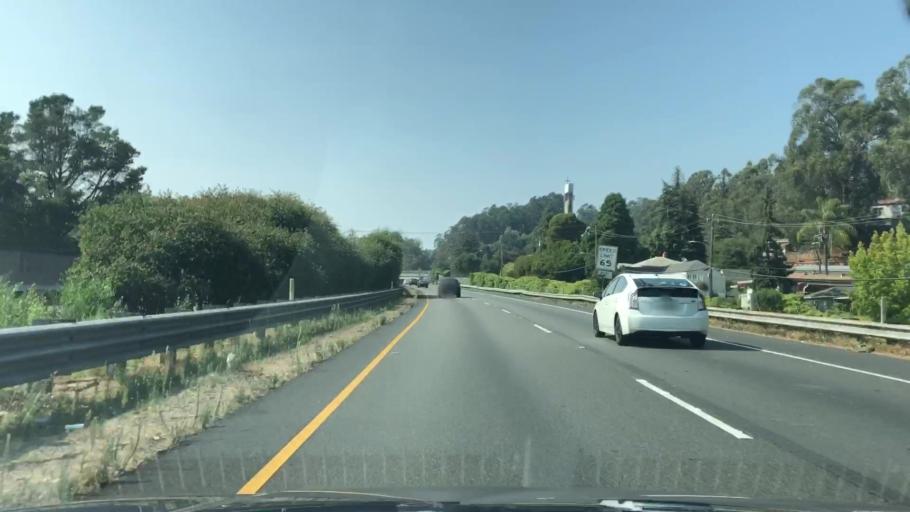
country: US
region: California
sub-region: Alameda County
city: Piedmont
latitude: 37.7946
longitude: -122.1822
